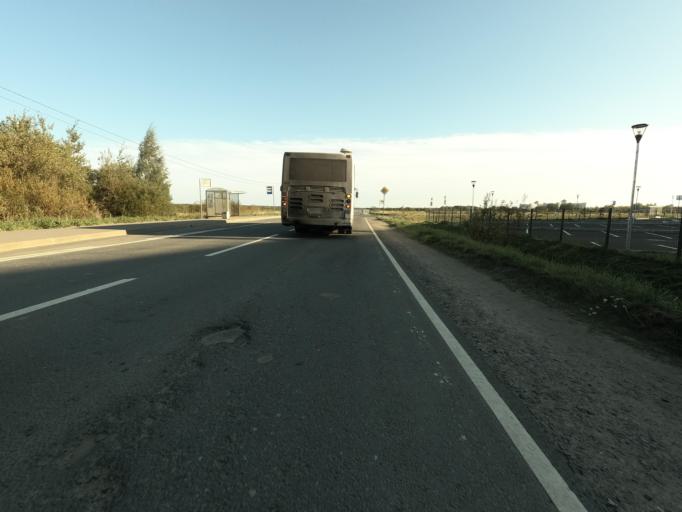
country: RU
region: St.-Petersburg
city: Pontonnyy
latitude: 59.7550
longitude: 30.6320
